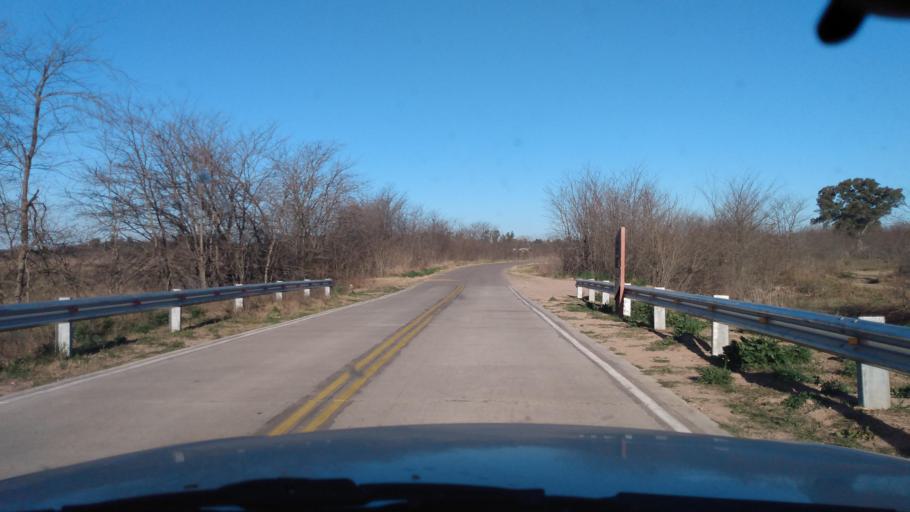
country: AR
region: Buenos Aires
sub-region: Partido de Lujan
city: Lujan
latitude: -34.6174
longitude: -59.2601
